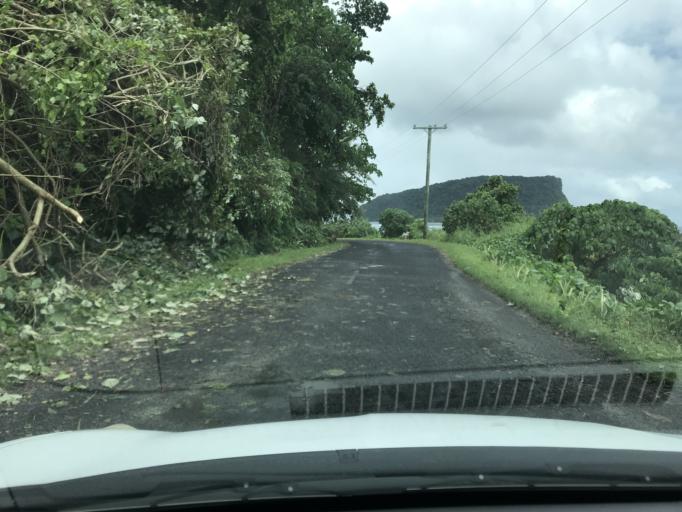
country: WS
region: Va`a-o-Fonoti
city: Samamea
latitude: -14.0464
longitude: -171.4435
